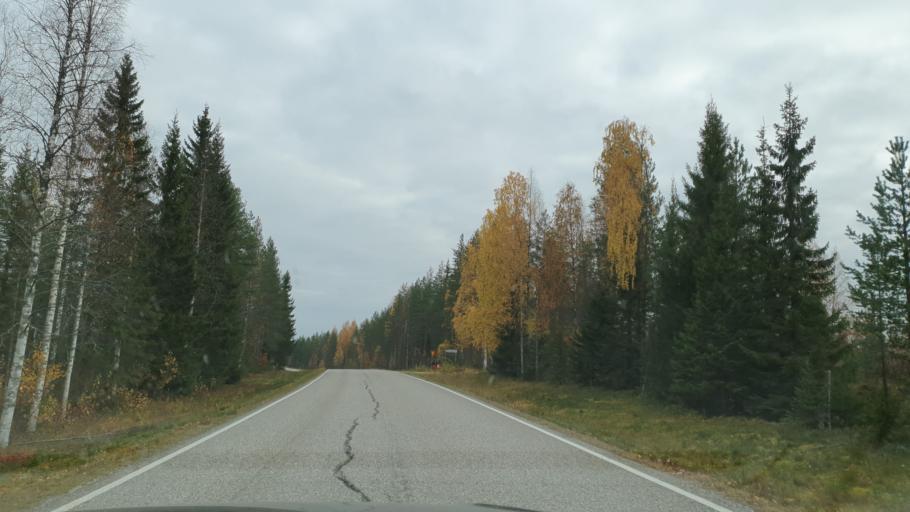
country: FI
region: Kainuu
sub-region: Kajaani
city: Ristijaervi
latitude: 64.6040
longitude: 28.0063
